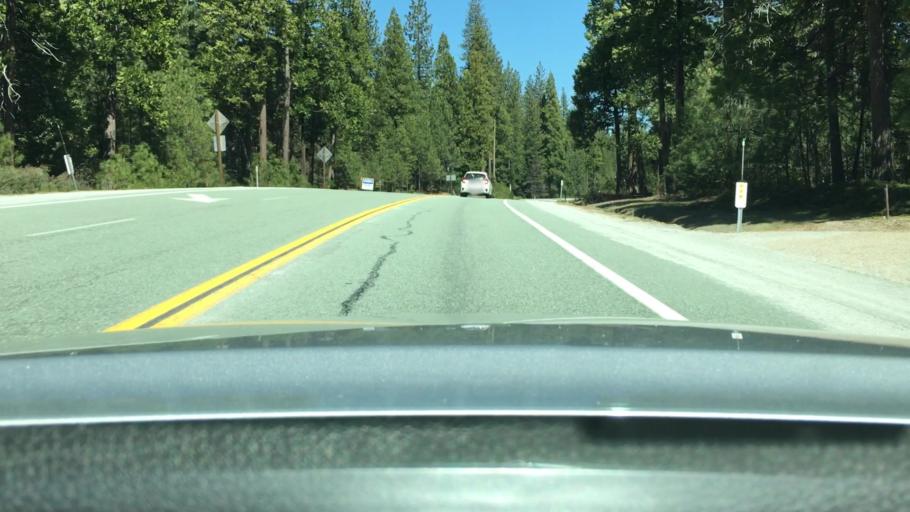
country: US
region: California
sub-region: Amador County
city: Pioneer
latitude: 38.4867
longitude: -120.5176
